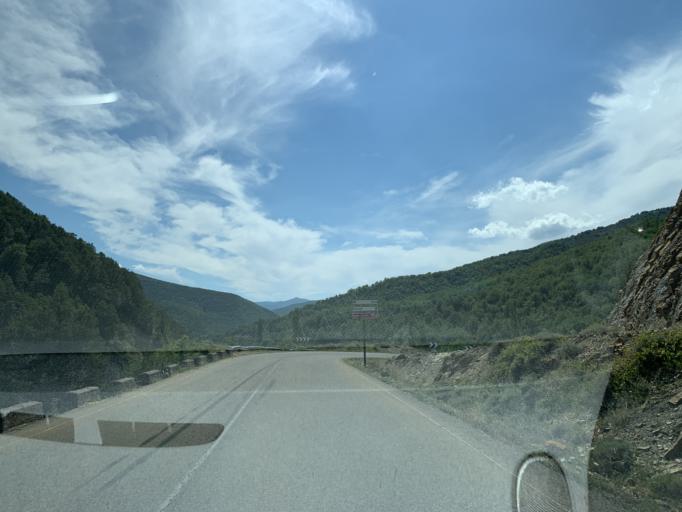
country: ES
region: Aragon
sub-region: Provincia de Huesca
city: Jasa
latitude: 42.6458
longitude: -0.6422
